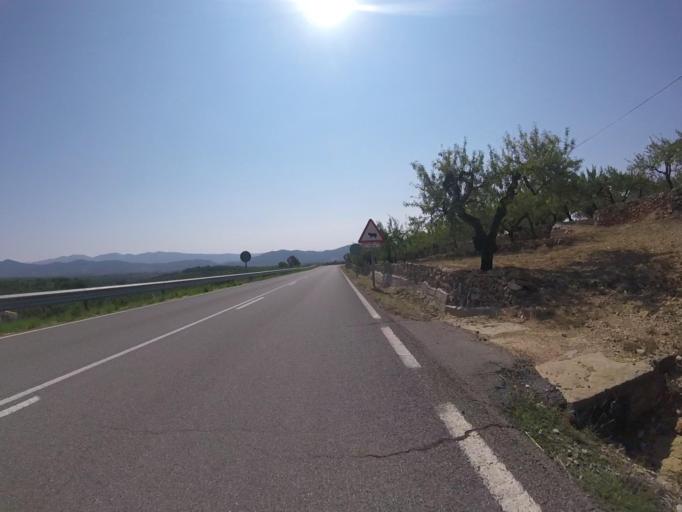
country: ES
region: Valencia
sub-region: Provincia de Castello
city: Adzaneta
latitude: 40.2426
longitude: -0.1911
